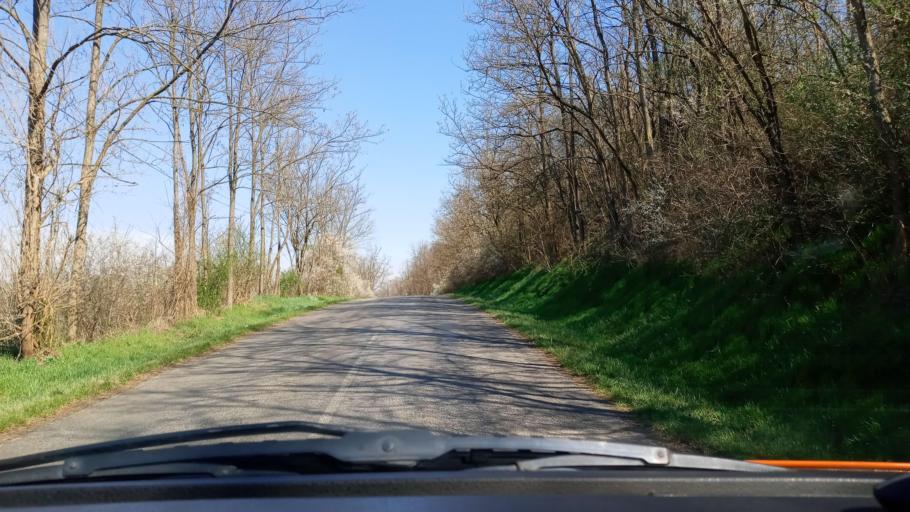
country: HU
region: Baranya
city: Boly
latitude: 46.0541
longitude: 18.4568
